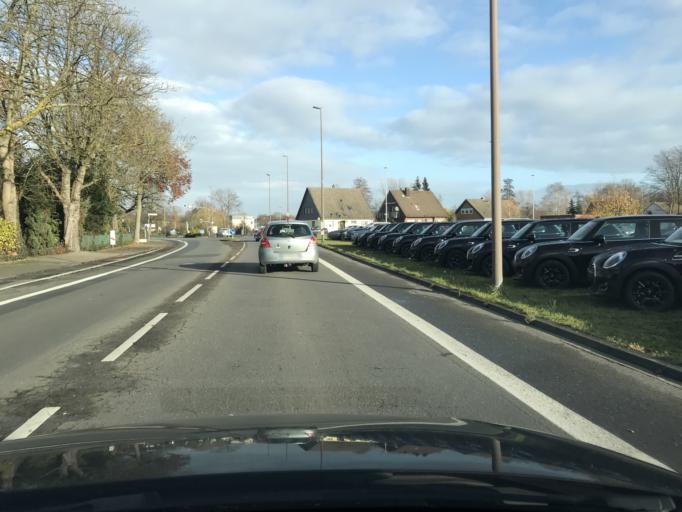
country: DE
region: North Rhine-Westphalia
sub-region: Regierungsbezirk Arnsberg
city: Hamm
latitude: 51.6786
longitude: 7.8522
